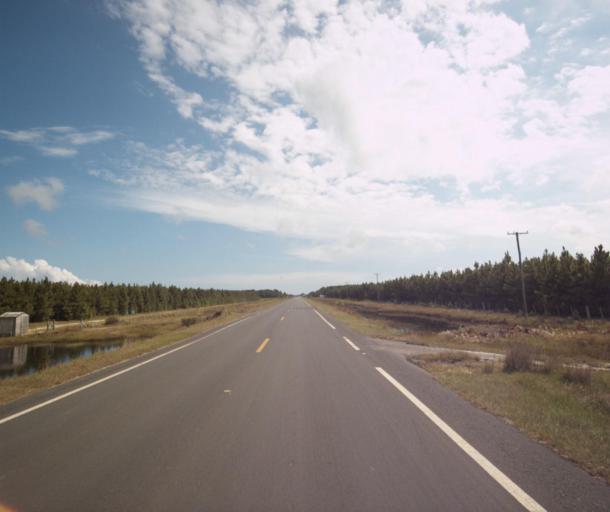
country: BR
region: Rio Grande do Sul
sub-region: Sao Lourenco Do Sul
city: Sao Lourenco do Sul
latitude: -31.5963
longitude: -51.3750
